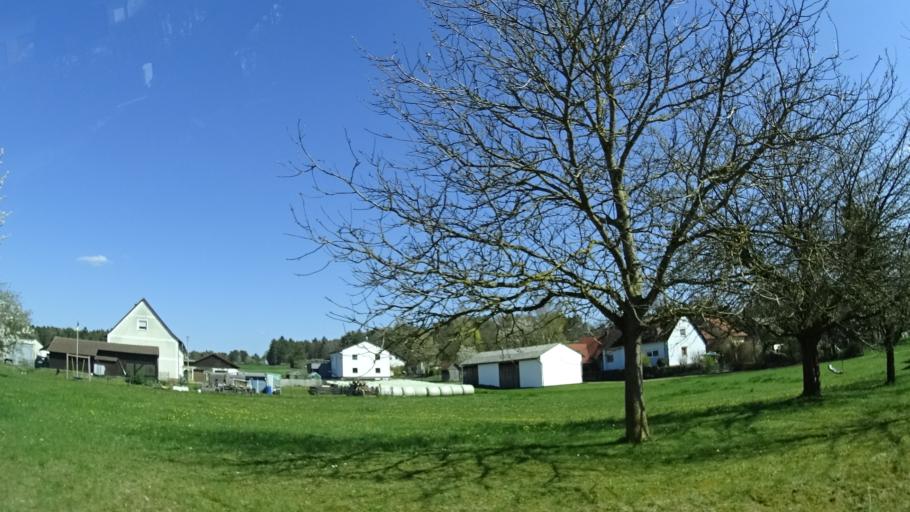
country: DE
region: Bavaria
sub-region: Upper Palatinate
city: Illschwang
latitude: 49.4910
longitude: 11.6498
